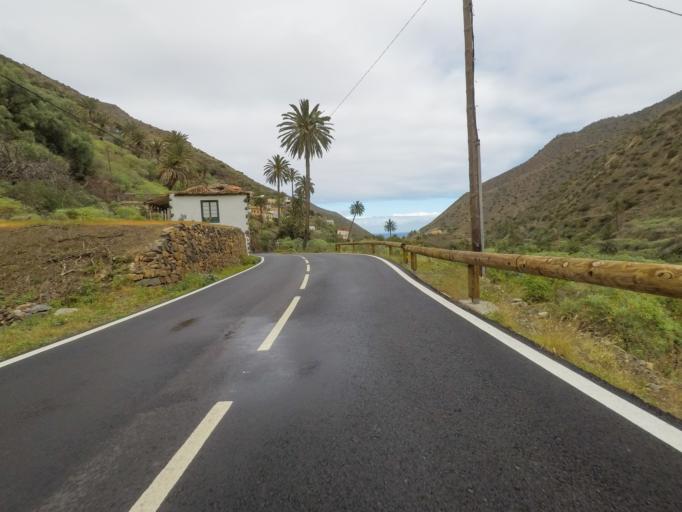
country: ES
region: Canary Islands
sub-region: Provincia de Santa Cruz de Tenerife
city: Vallehermosa
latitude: 28.1862
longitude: -17.2640
